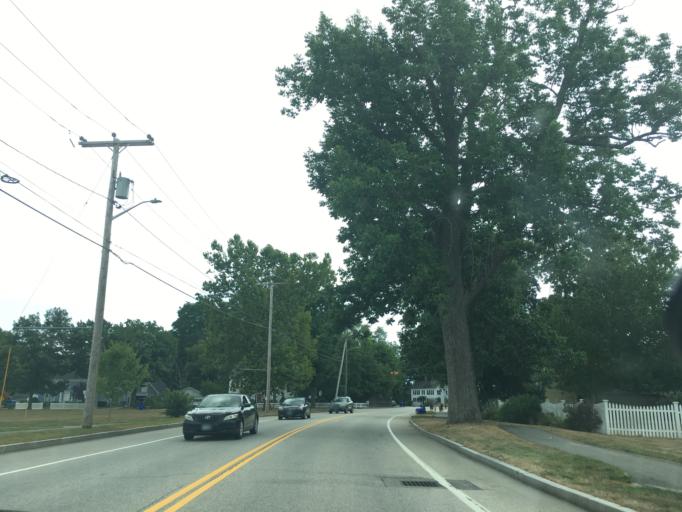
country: US
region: New Hampshire
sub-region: Rockingham County
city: Exeter
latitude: 42.9843
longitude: -70.9602
